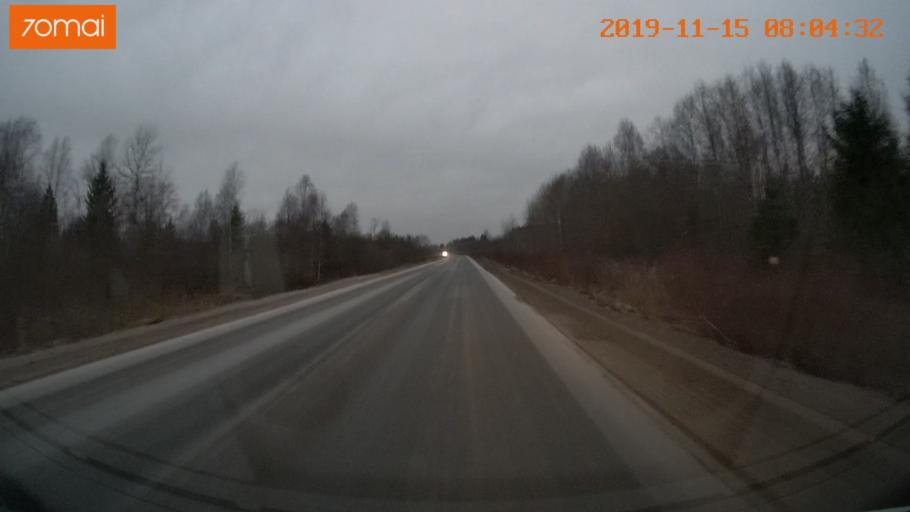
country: RU
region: Vologda
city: Cherepovets
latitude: 59.0092
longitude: 38.0743
